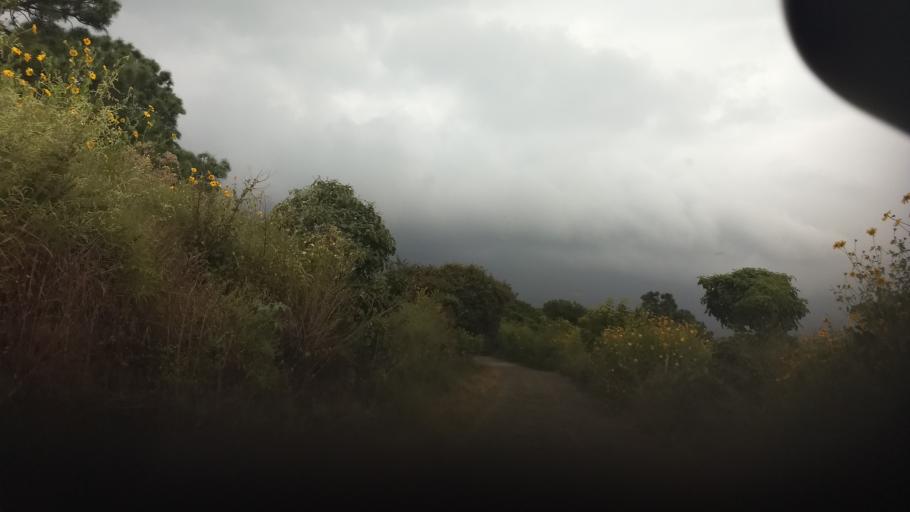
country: MX
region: Jalisco
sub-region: Tonila
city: San Marcos
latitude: 19.4661
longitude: -103.5341
